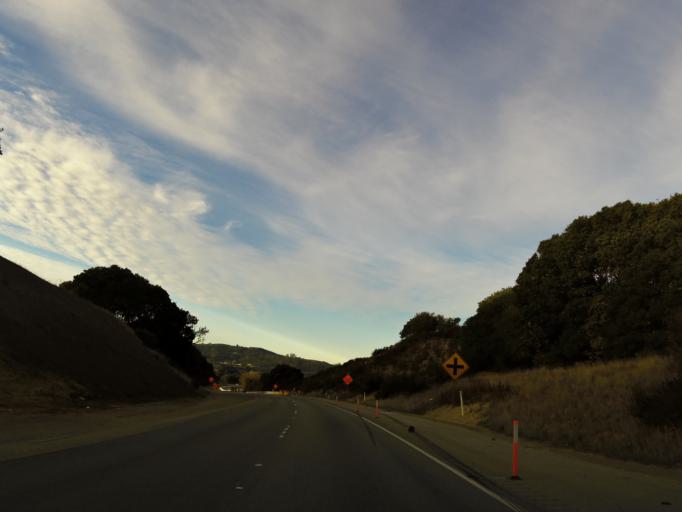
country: US
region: California
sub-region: San Benito County
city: Aromas
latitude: 36.8629
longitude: -121.6198
